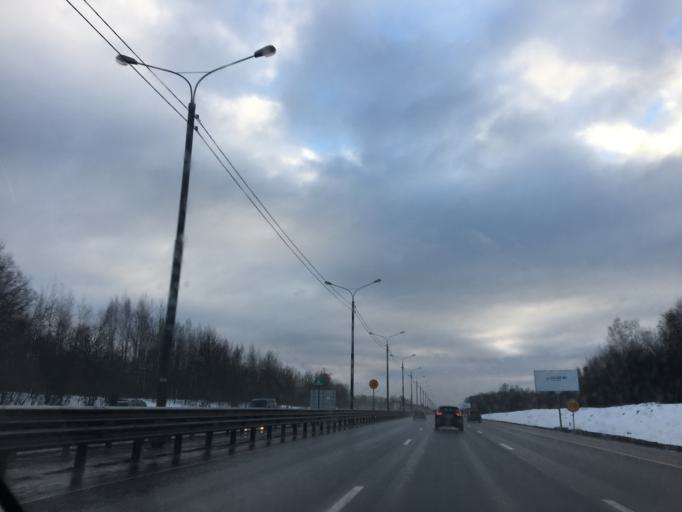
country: RU
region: Moskovskaya
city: L'vovskiy
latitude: 55.3220
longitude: 37.5591
